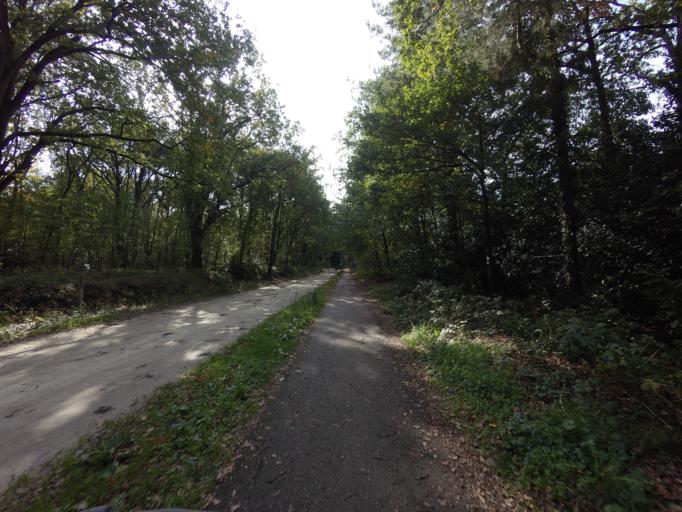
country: NL
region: North Brabant
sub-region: Gemeente Breda
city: Hoge Vucht
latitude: 51.6014
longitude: 4.8290
